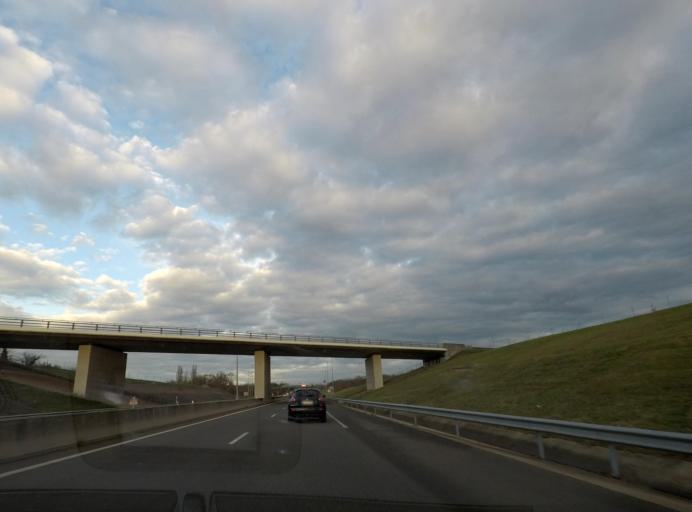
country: FR
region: Rhone-Alpes
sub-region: Departement de l'Ain
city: Crottet
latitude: 46.2939
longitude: 4.8941
